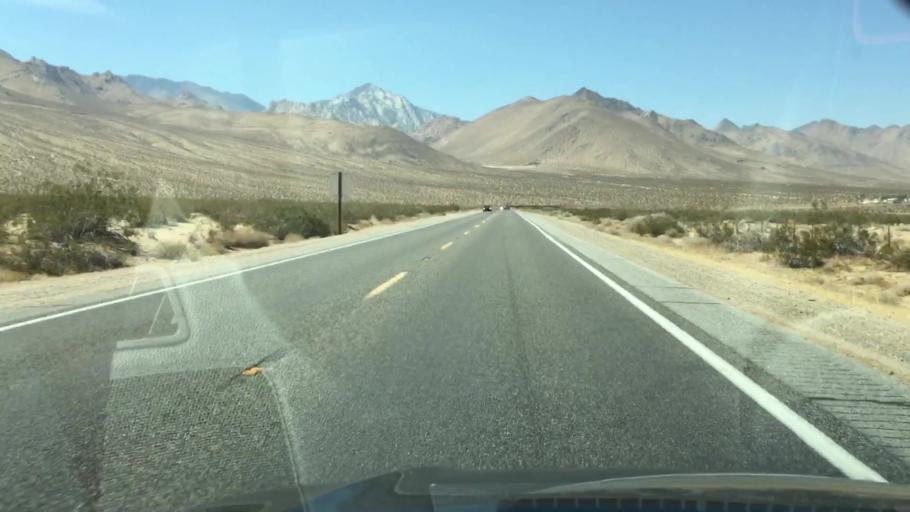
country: US
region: California
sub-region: Kern County
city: Inyokern
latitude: 35.6886
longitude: -117.8563
